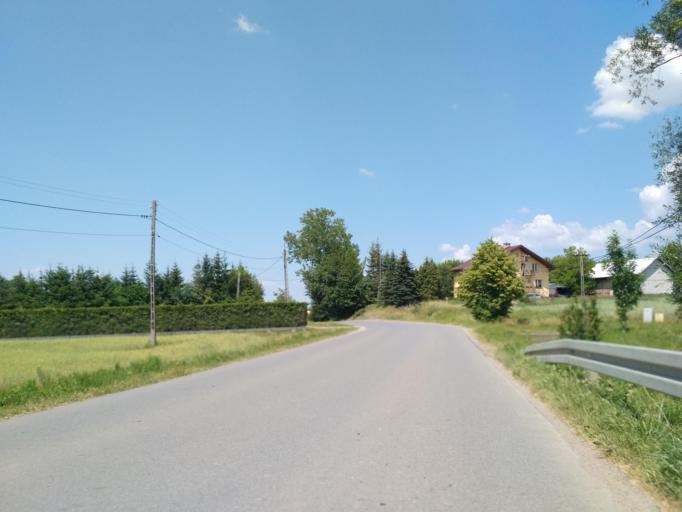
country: PL
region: Subcarpathian Voivodeship
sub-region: Powiat sanocki
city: Niebieszczany
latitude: 49.5078
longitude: 22.1545
